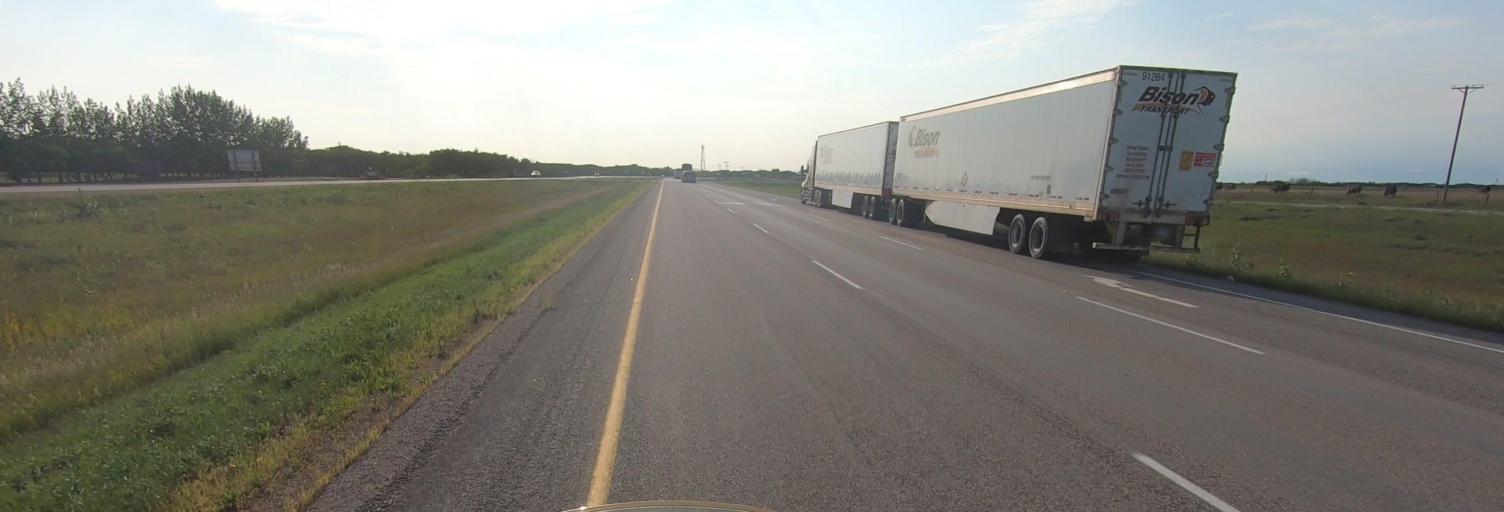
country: CA
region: Saskatchewan
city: Esterhazy
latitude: 50.3379
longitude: -102.2778
